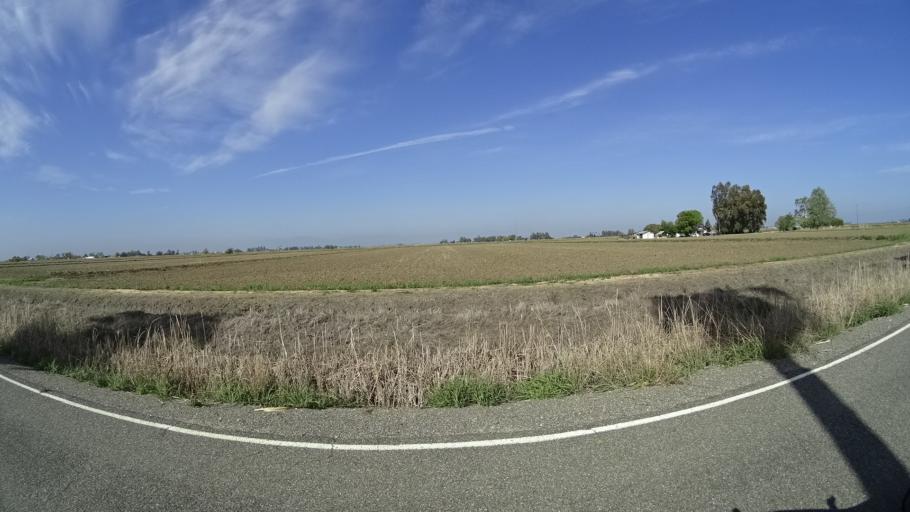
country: US
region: California
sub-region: Glenn County
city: Hamilton City
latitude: 39.5929
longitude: -122.0368
